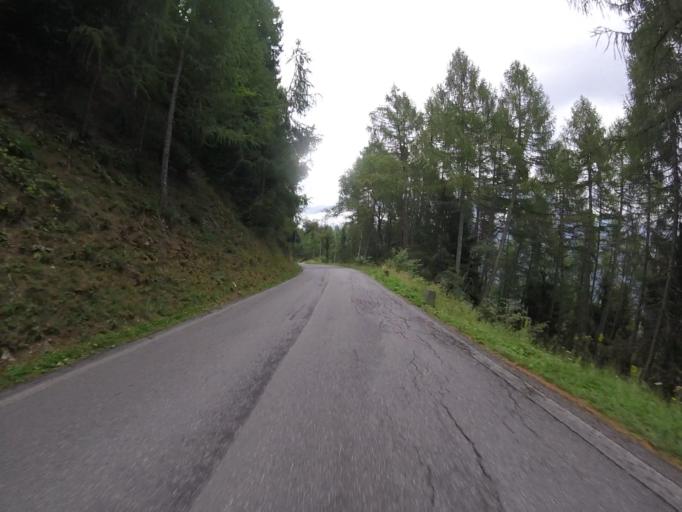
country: IT
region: Lombardy
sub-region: Provincia di Brescia
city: Monno
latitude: 46.2195
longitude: 10.3304
